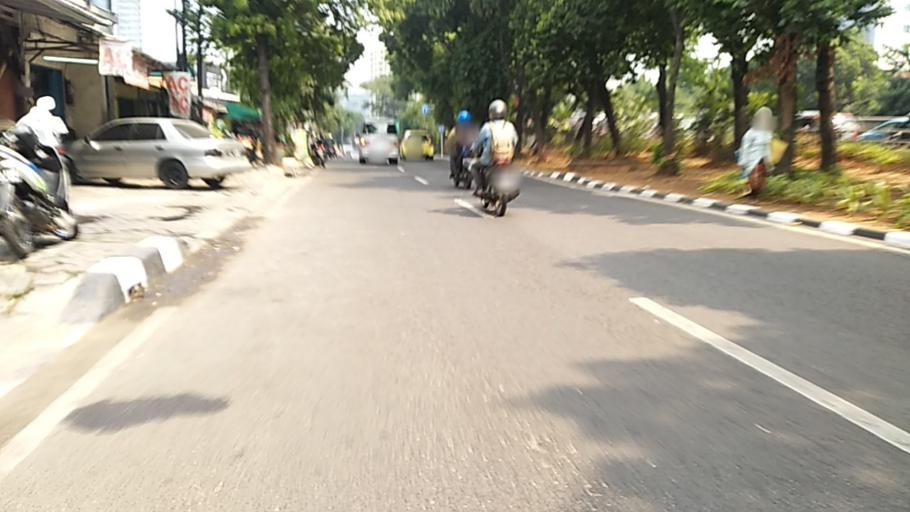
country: ID
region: Jakarta Raya
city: Jakarta
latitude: -6.2238
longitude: 106.8491
